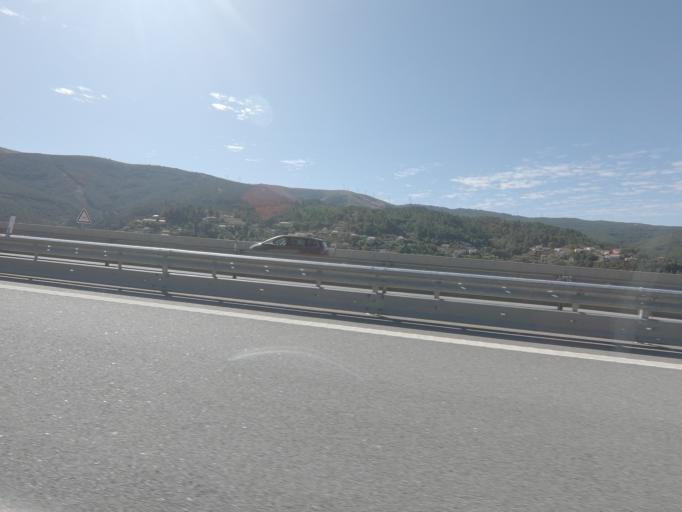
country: PT
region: Viseu
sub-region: Mangualde
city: Mangualde
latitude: 40.6136
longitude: -7.6941
